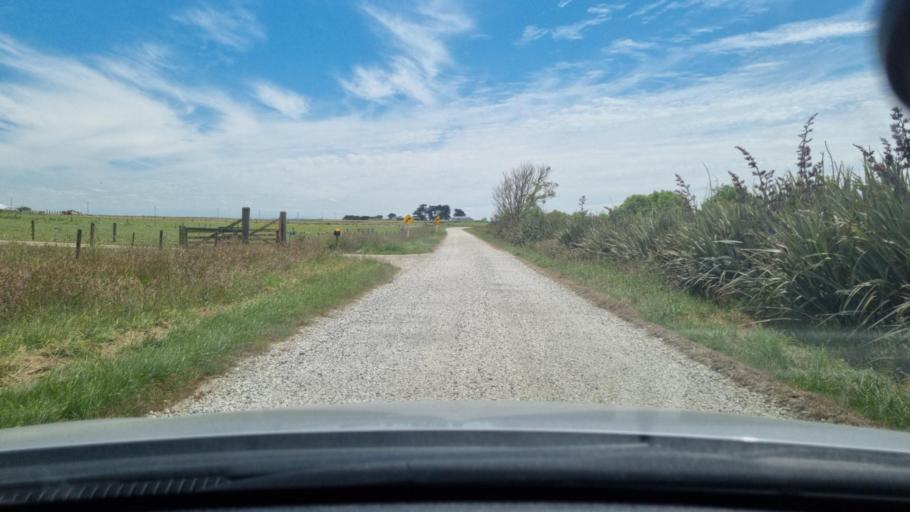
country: NZ
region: Southland
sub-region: Invercargill City
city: Invercargill
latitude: -46.4041
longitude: 168.2596
